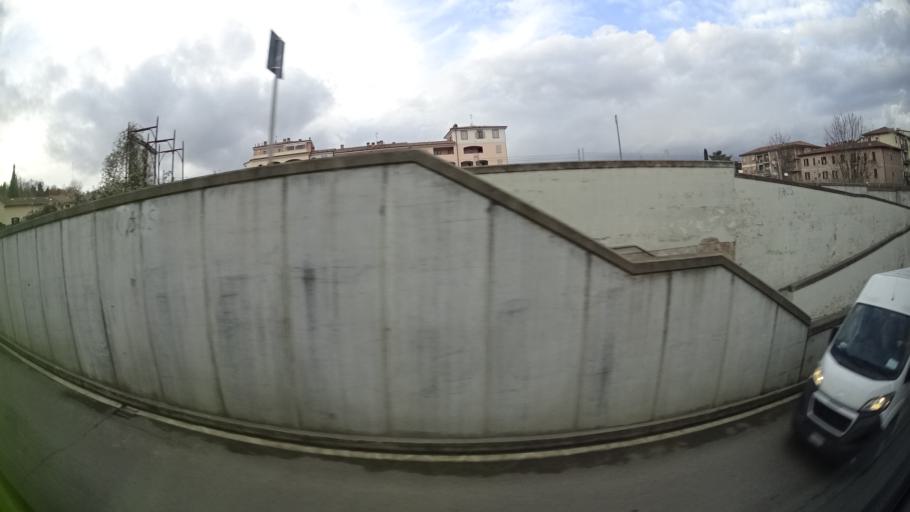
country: IT
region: Tuscany
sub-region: Provincia di Siena
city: Poggibonsi
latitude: 43.4663
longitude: 11.1512
